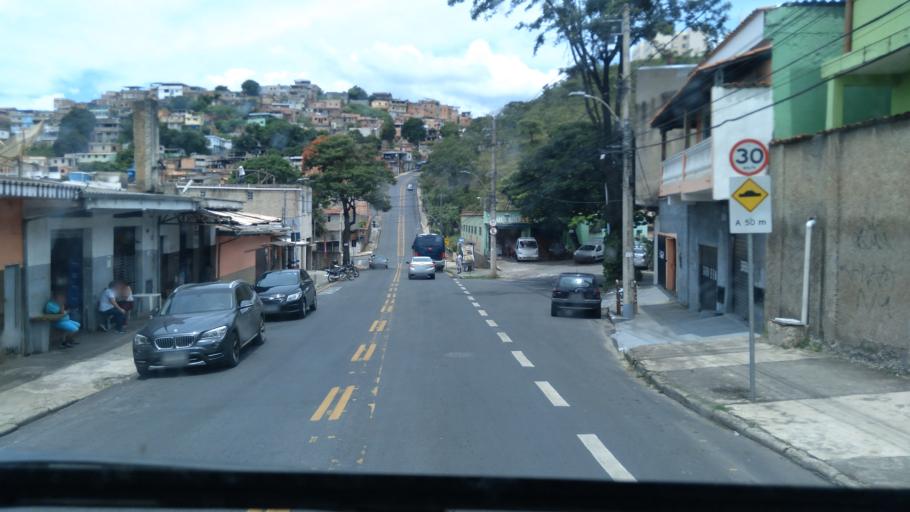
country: BR
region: Minas Gerais
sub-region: Belo Horizonte
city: Belo Horizonte
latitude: -19.9179
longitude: -43.8919
